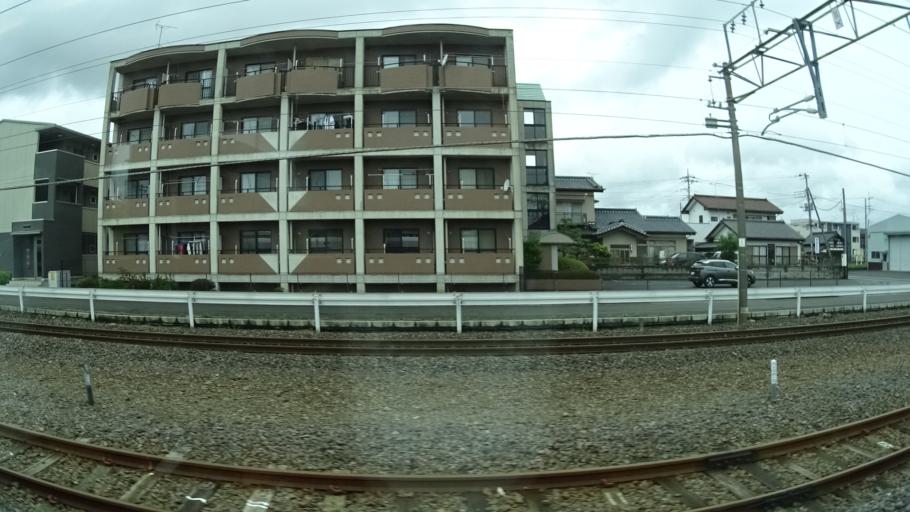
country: JP
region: Ibaraki
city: Funaishikawa
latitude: 36.4633
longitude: 140.5633
